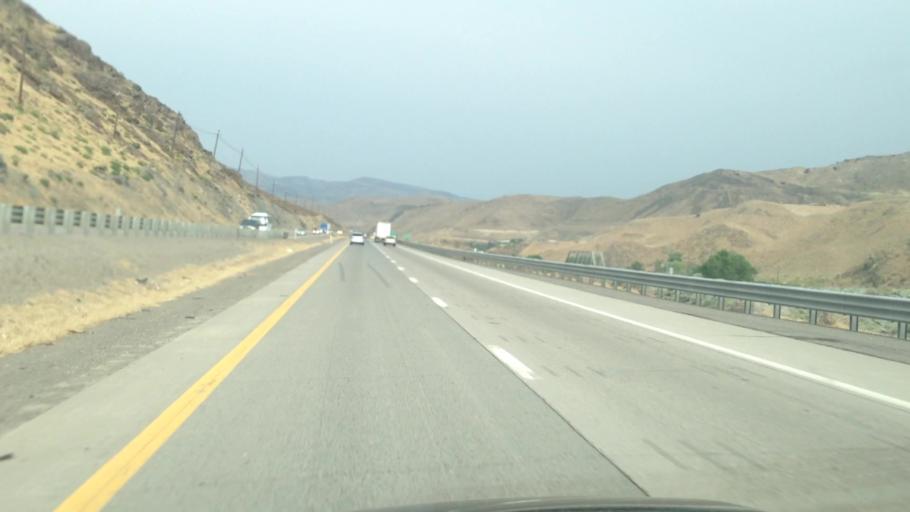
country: US
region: Nevada
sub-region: Washoe County
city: Sparks
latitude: 39.5128
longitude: -119.6742
